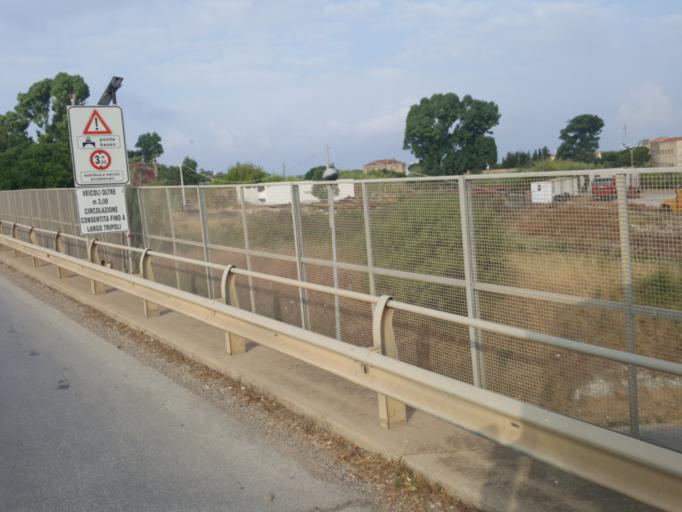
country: IT
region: Latium
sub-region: Citta metropolitana di Roma Capitale
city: Civitavecchia
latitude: 42.1035
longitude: 11.7927
